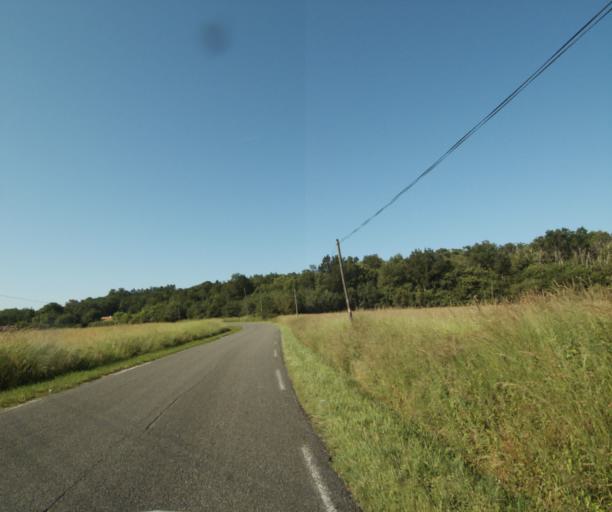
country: FR
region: Midi-Pyrenees
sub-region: Departement du Tarn-et-Garonne
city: Saint-Etienne-de-Tulmont
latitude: 44.0260
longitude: 1.4265
